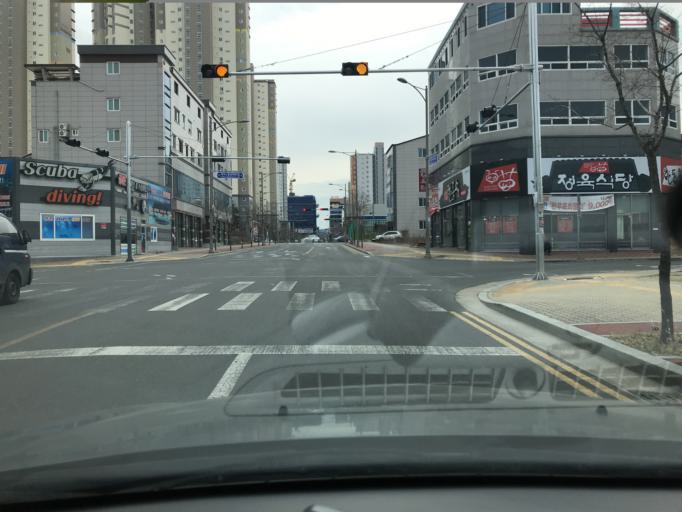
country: KR
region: Daegu
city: Hwawon
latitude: 35.6976
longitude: 128.4544
